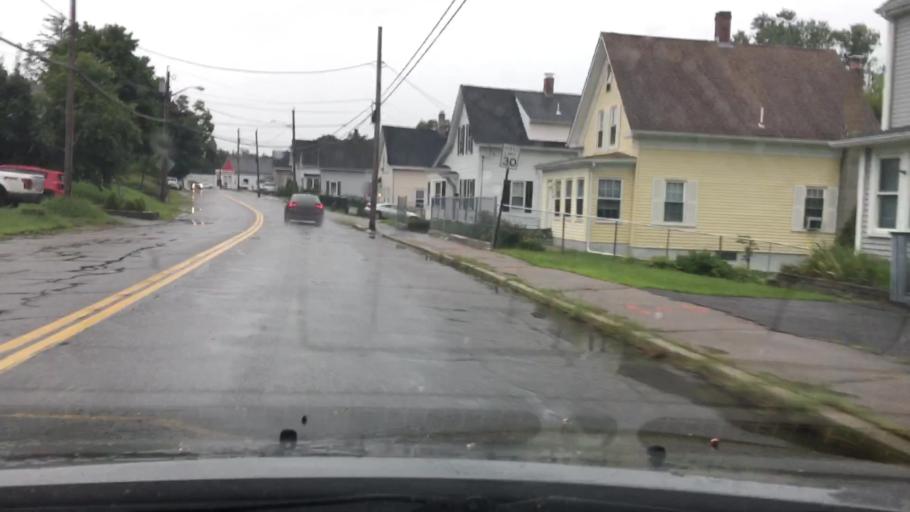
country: US
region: Massachusetts
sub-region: Worcester County
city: Milford
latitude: 42.1334
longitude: -71.5208
